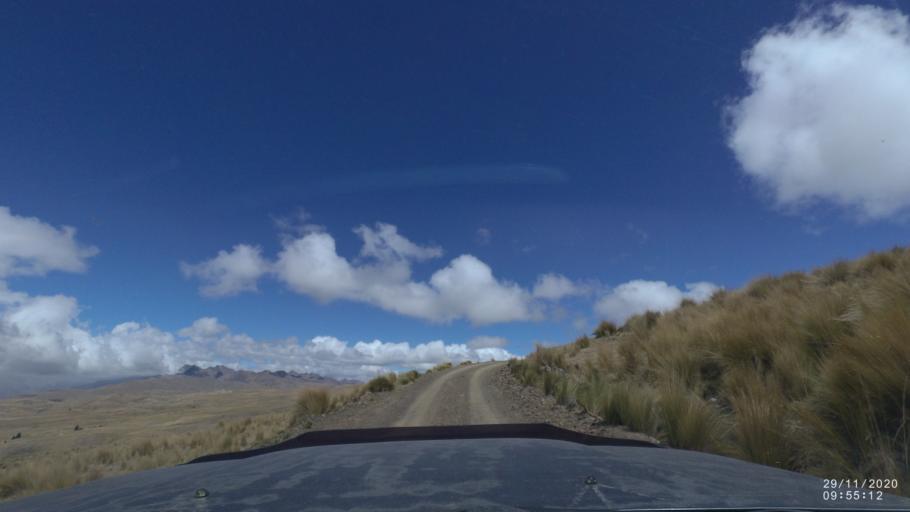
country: BO
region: Cochabamba
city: Cochabamba
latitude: -17.2758
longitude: -66.1786
